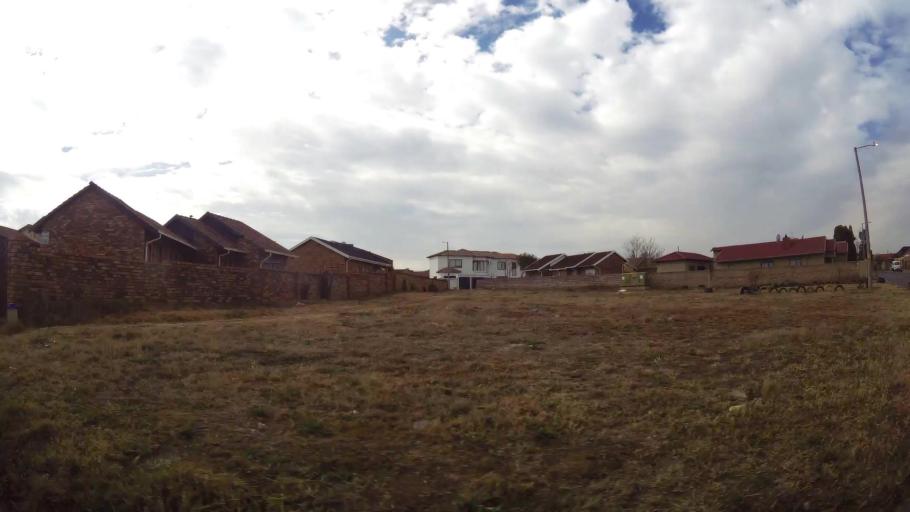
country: ZA
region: Gauteng
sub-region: Ekurhuleni Metropolitan Municipality
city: Germiston
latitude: -26.3238
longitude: 28.1800
